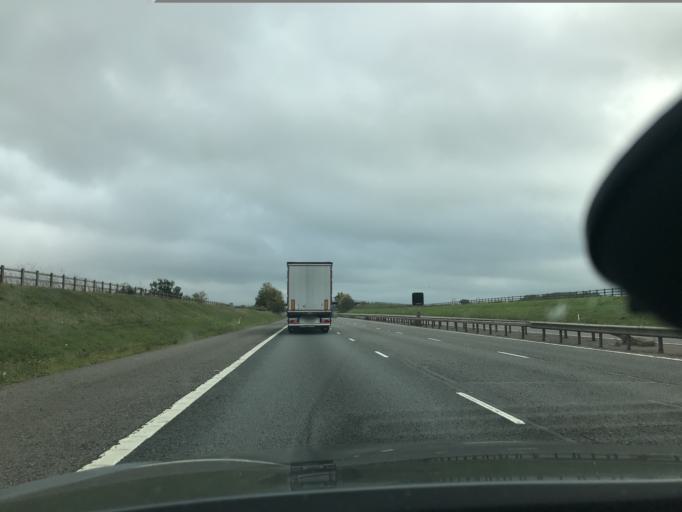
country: GB
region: England
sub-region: Warwickshire
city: Warwick
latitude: 52.2496
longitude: -1.5705
